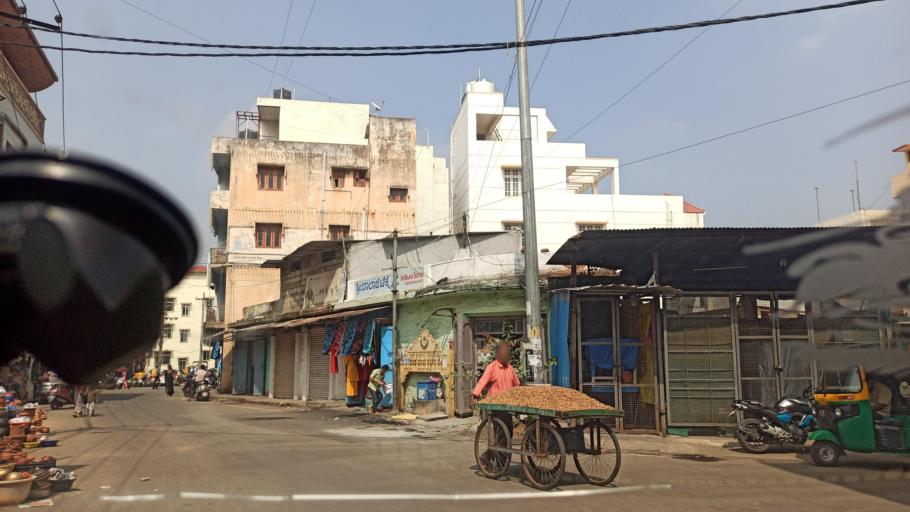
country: IN
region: Karnataka
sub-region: Bangalore Urban
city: Yelahanka
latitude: 13.1018
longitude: 77.5948
